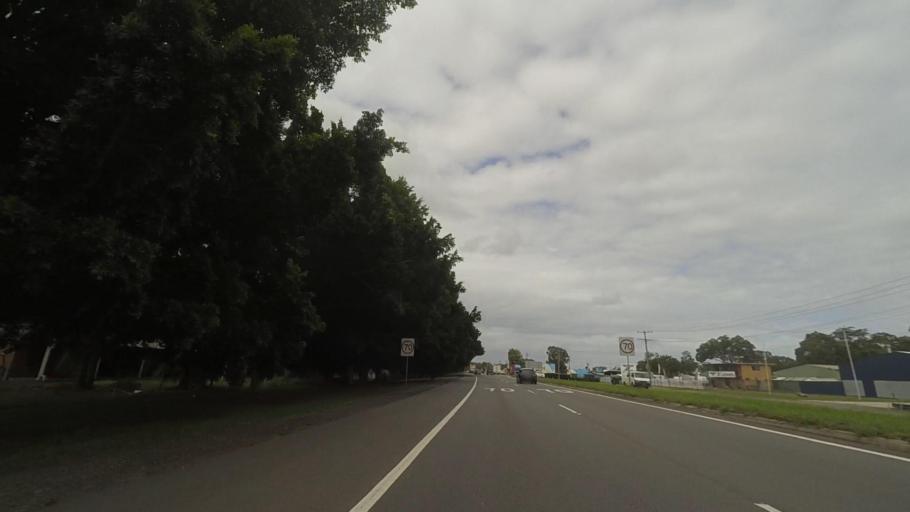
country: AU
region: New South Wales
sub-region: Port Stephens Shire
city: Raymond Terrace
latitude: -32.7867
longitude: 151.7305
